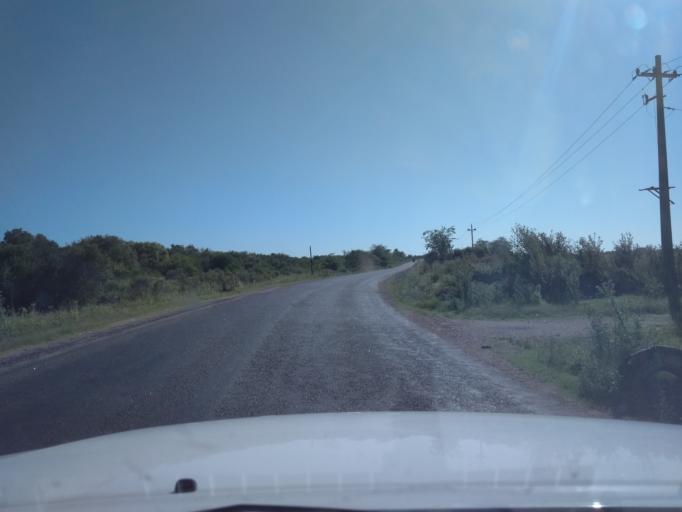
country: UY
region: Canelones
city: San Ramon
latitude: -34.2694
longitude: -55.9397
